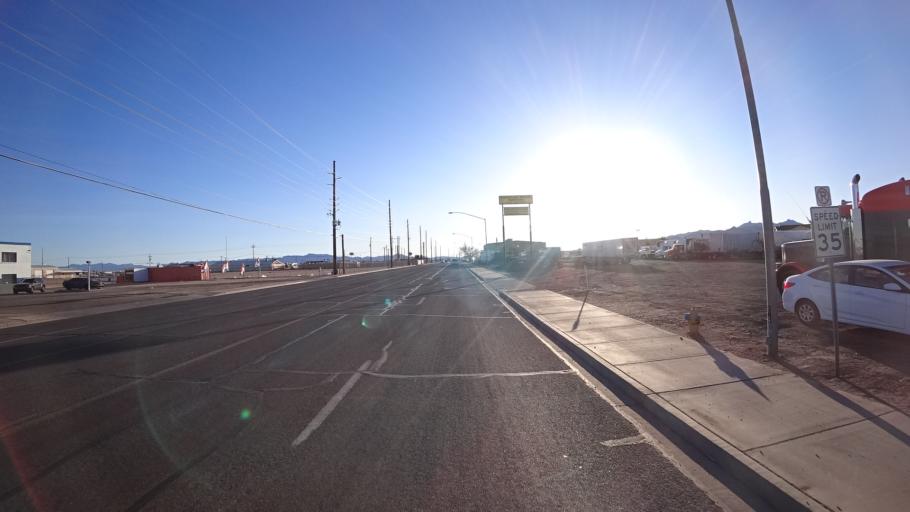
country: US
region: Arizona
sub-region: Mohave County
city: New Kingman-Butler
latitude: 35.2248
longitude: -114.0075
